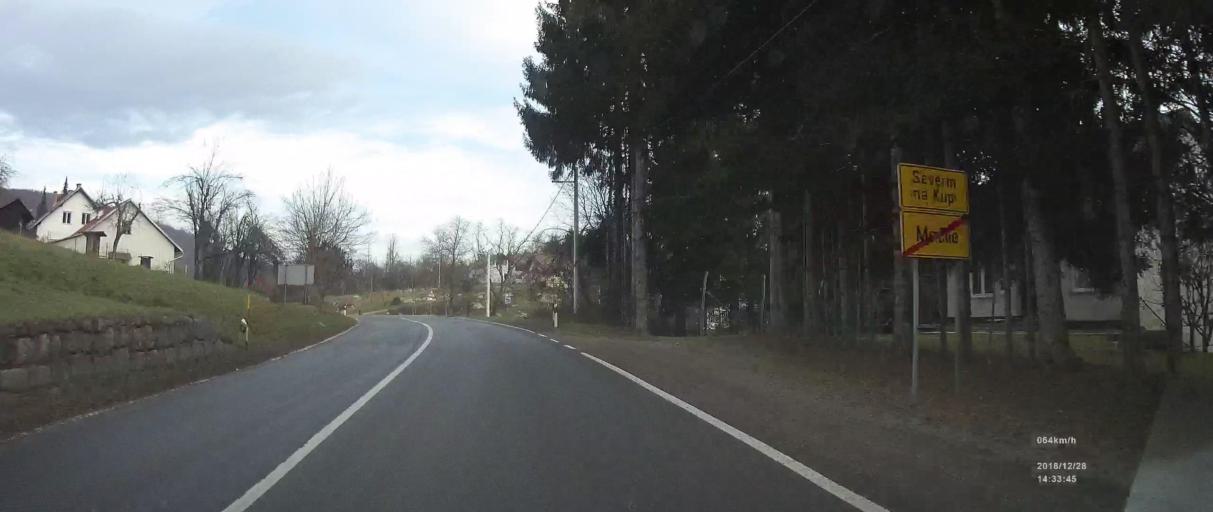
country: HR
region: Primorsko-Goranska
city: Vrbovsko
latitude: 45.4158
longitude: 15.1679
